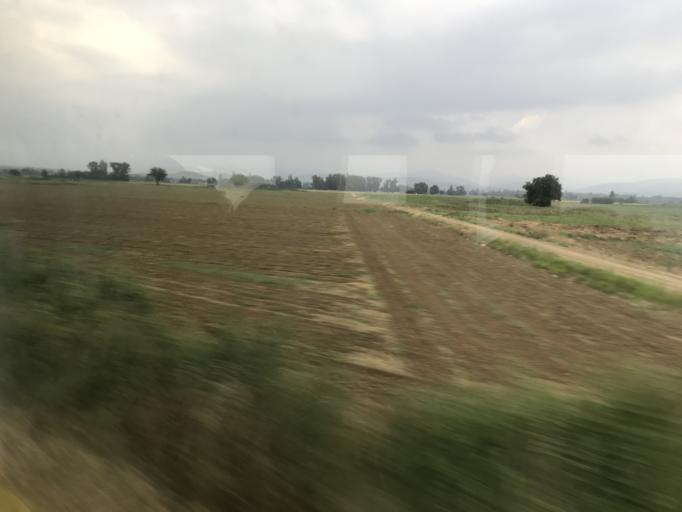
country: GR
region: East Macedonia and Thrace
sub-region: Nomos Rodopis
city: Arisvi
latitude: 41.0779
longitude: 25.5720
